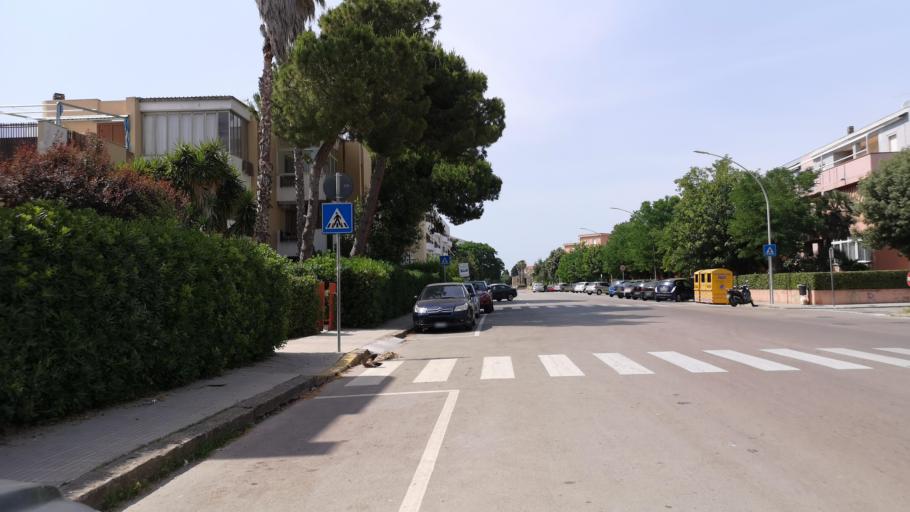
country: IT
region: Sardinia
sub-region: Provincia di Sassari
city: Alghero
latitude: 40.5775
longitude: 8.3157
